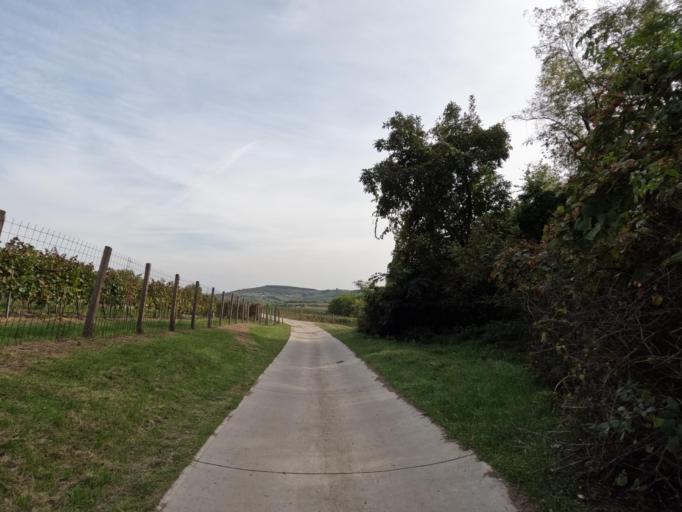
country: HU
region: Tolna
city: Szentgalpuszta
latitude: 46.3400
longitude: 18.6474
